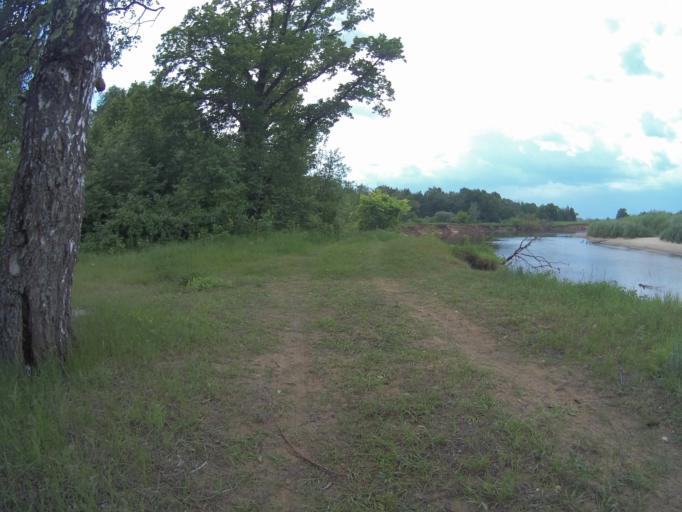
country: RU
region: Vladimir
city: Vorsha
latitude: 56.0340
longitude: 40.1996
